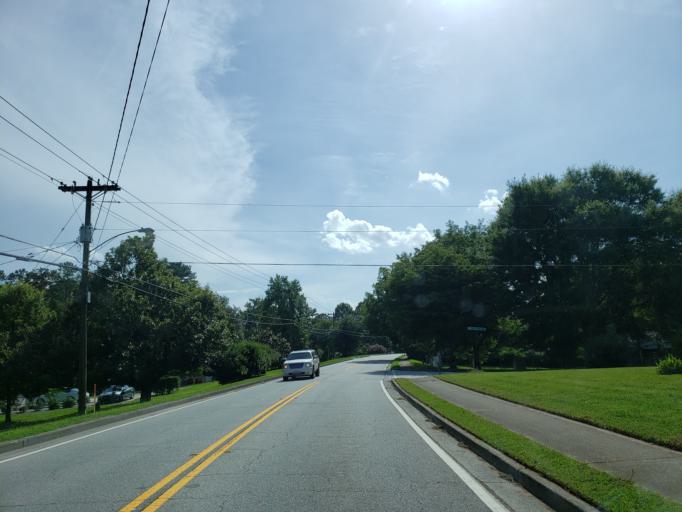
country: US
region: Georgia
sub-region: Cobb County
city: Mableton
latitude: 33.8638
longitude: -84.5713
